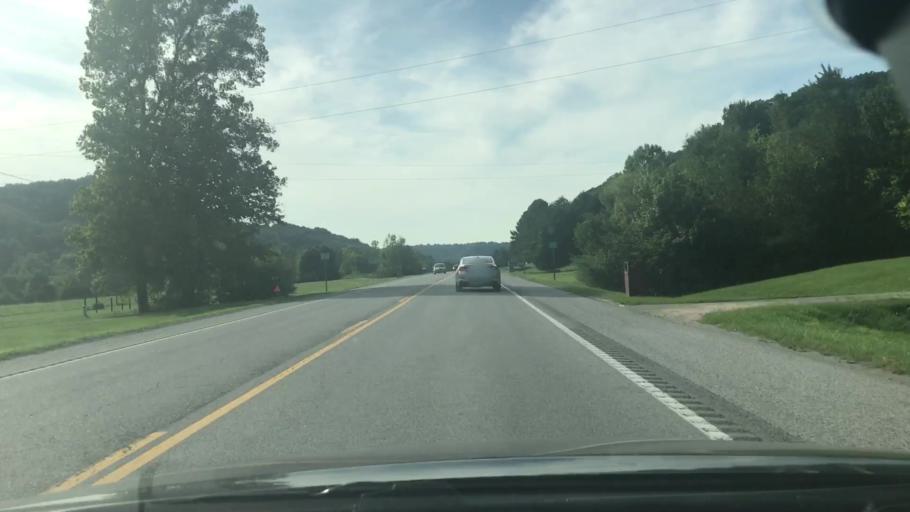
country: US
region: Tennessee
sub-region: Williamson County
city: Fairview
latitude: 35.9918
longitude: -87.0039
